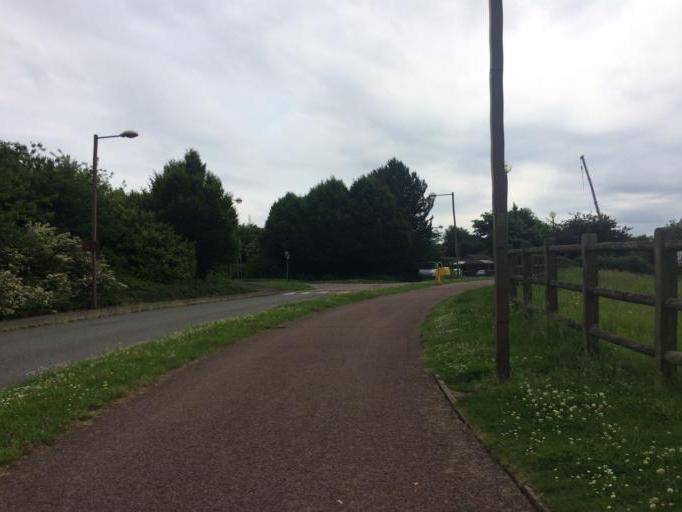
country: GB
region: England
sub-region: Milton Keynes
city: Loughton
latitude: 52.0288
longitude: -0.7748
